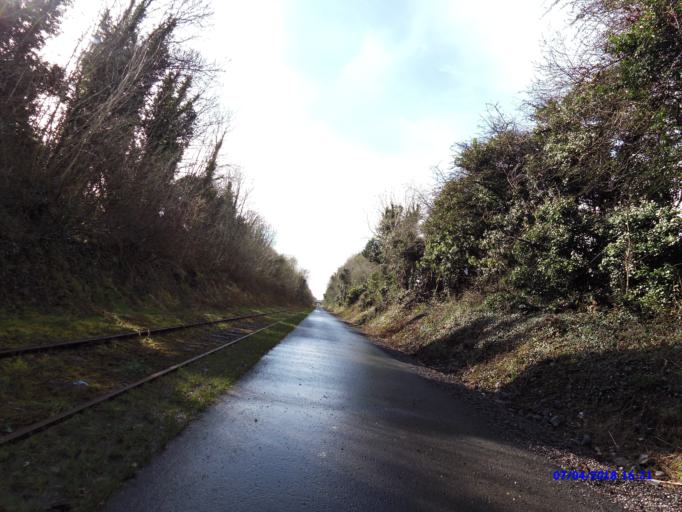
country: IE
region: Leinster
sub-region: An Iarmhi
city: Athlone
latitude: 53.4211
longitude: -7.8925
